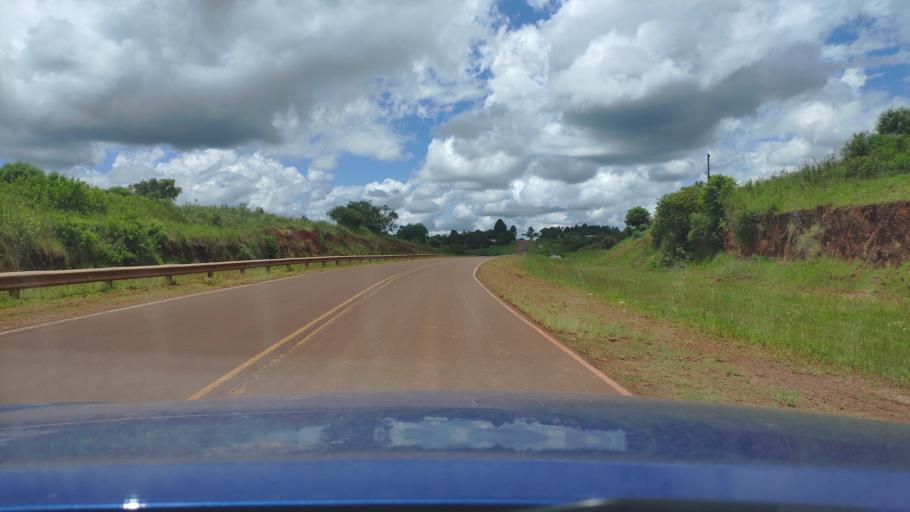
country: AR
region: Misiones
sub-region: Departamento de San Javier
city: San Javier
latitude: -27.8401
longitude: -55.2304
